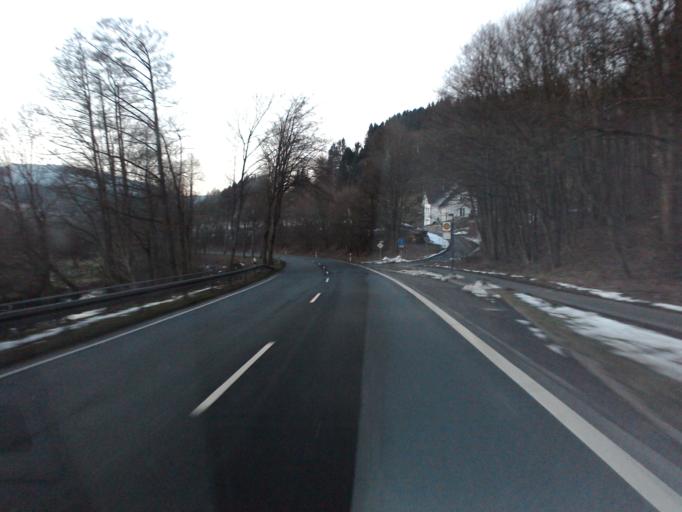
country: DE
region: North Rhine-Westphalia
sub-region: Regierungsbezirk Arnsberg
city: Olsberg
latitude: 51.3127
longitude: 8.5033
